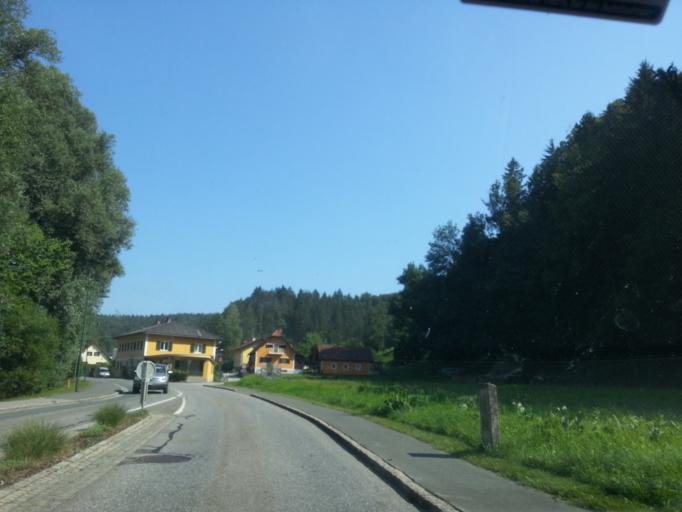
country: AT
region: Styria
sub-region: Politischer Bezirk Leibnitz
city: Grossklein
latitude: 46.7366
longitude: 15.4449
